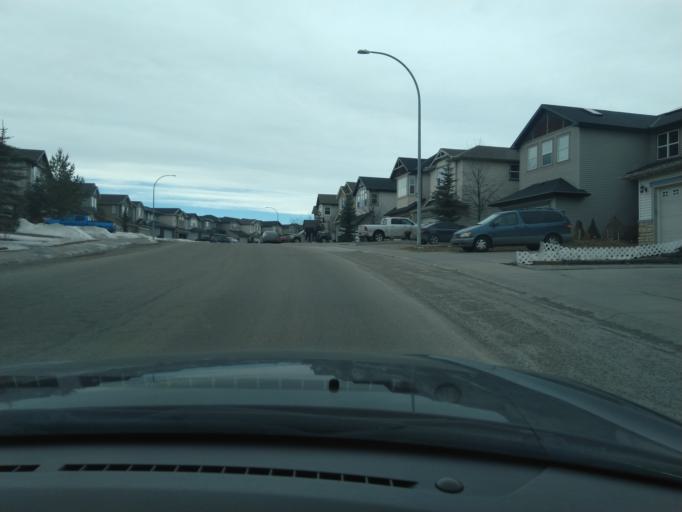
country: CA
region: Alberta
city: Calgary
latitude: 51.1643
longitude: -114.0965
